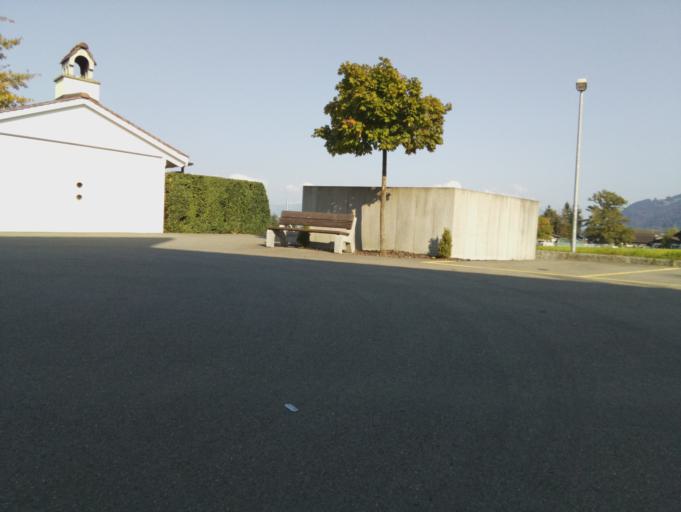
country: CH
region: Schwyz
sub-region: Bezirk March
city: Lachen
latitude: 47.1773
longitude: 8.8800
